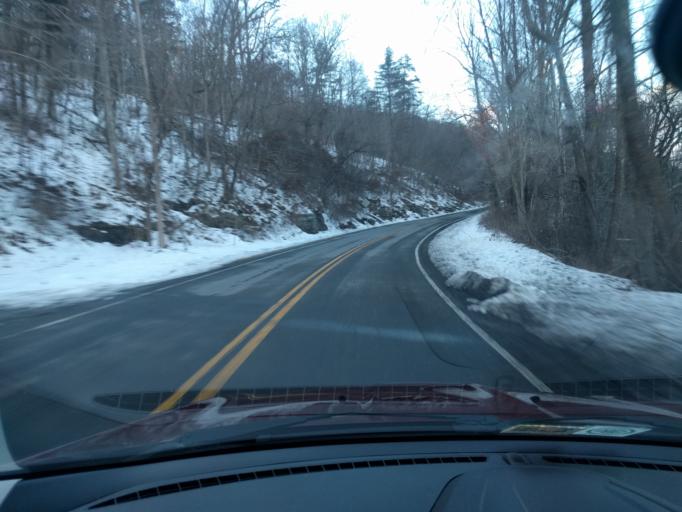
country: US
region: Virginia
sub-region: Bath County
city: Warm Springs
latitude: 38.0783
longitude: -79.8457
